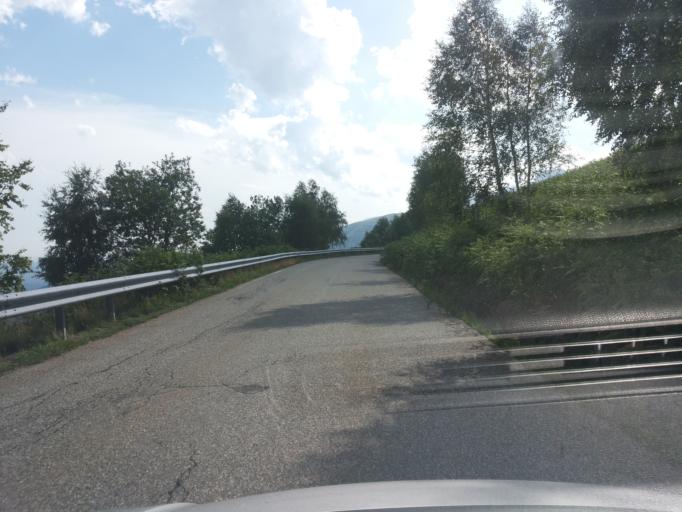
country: IT
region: Piedmont
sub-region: Provincia di Biella
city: Sagliano Micca
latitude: 45.6555
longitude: 8.0502
